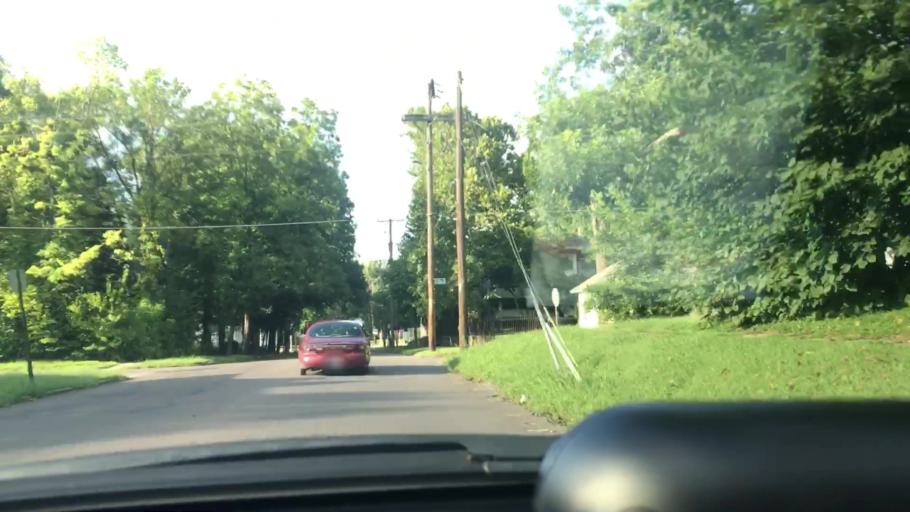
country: US
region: Missouri
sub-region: Pettis County
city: Sedalia
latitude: 38.7034
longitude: -93.2365
